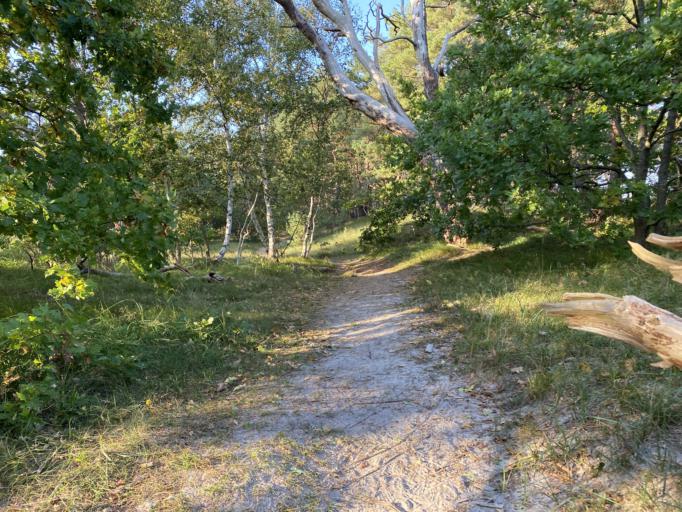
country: DE
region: Mecklenburg-Vorpommern
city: Ostseebad Binz
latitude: 54.4357
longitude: 13.5788
